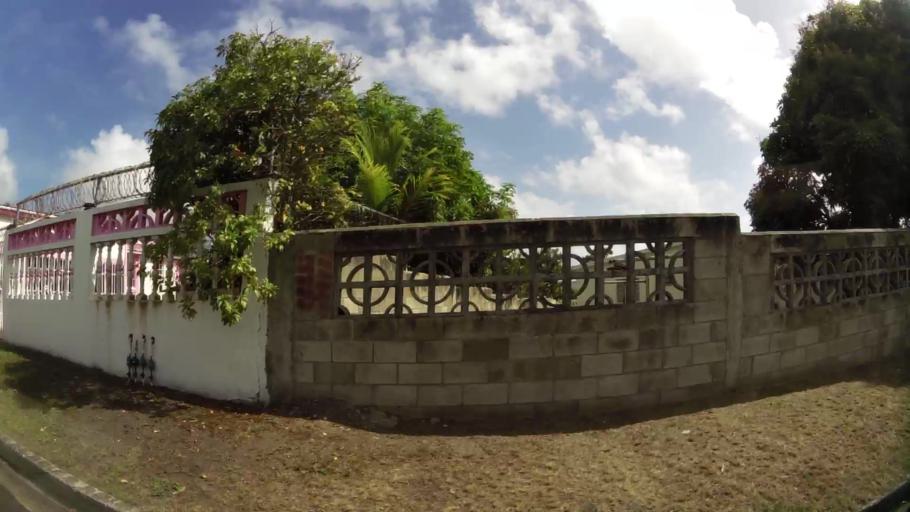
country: KN
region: Saint George Basseterre
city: Basseterre
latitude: 17.2997
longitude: -62.7285
